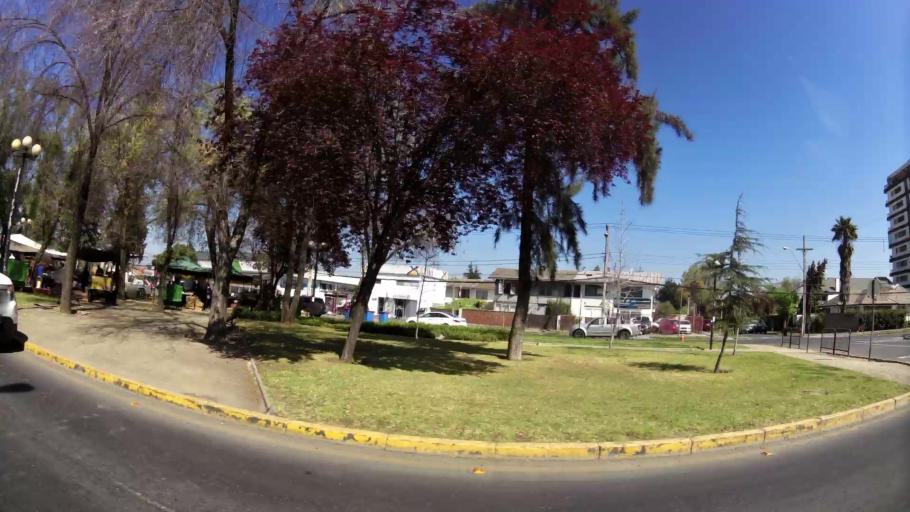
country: CL
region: Santiago Metropolitan
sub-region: Provincia de Santiago
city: Villa Presidente Frei, Nunoa, Santiago, Chile
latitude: -33.4242
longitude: -70.5641
